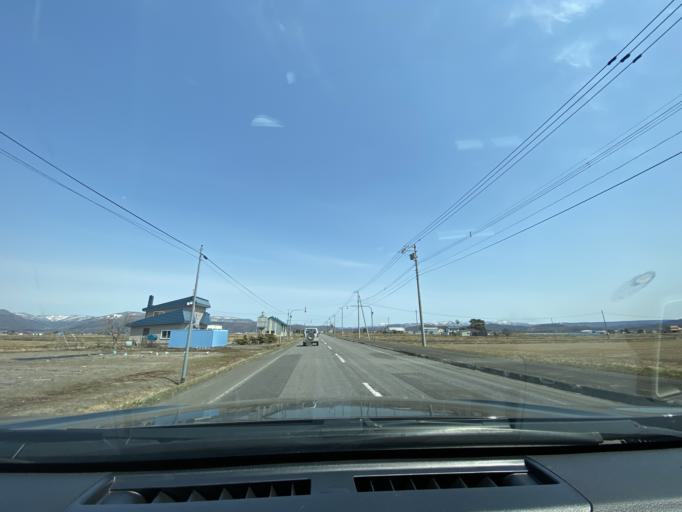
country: JP
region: Hokkaido
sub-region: Asahikawa-shi
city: Asahikawa
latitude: 43.8746
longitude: 142.4932
